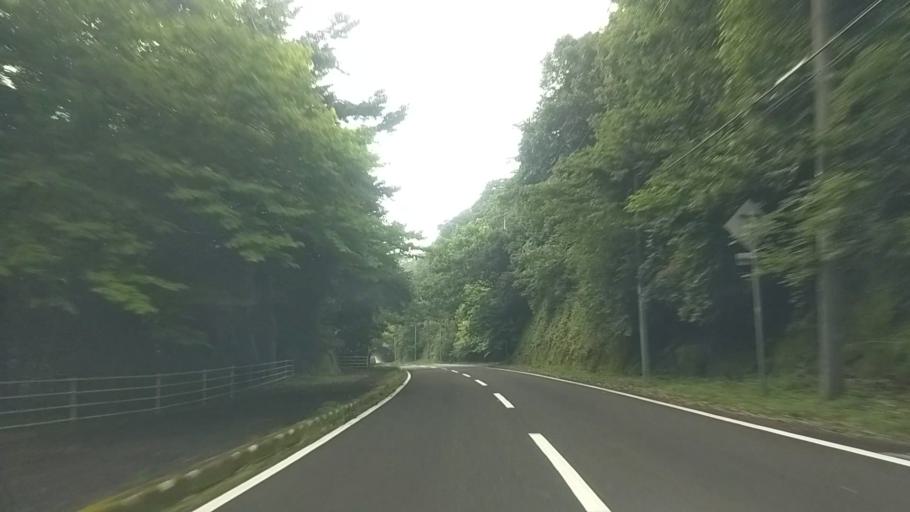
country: JP
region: Chiba
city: Kawaguchi
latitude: 35.1657
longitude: 140.1401
